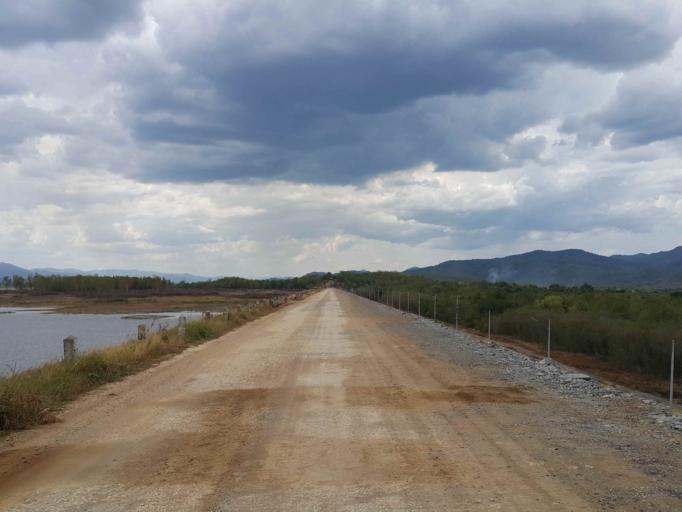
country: TH
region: Sukhothai
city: Thung Saliam
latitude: 17.3152
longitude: 99.4246
